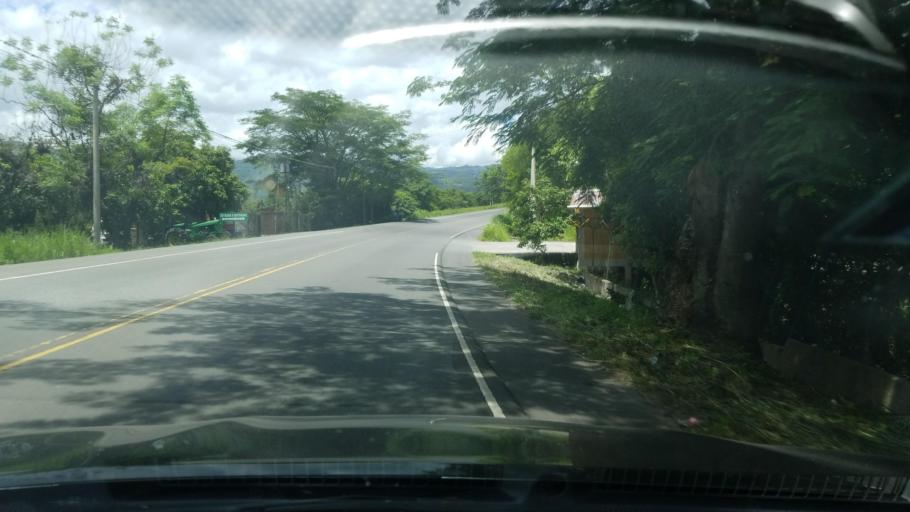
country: HN
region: Francisco Morazan
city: Cofradia
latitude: 14.1980
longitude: -87.2075
